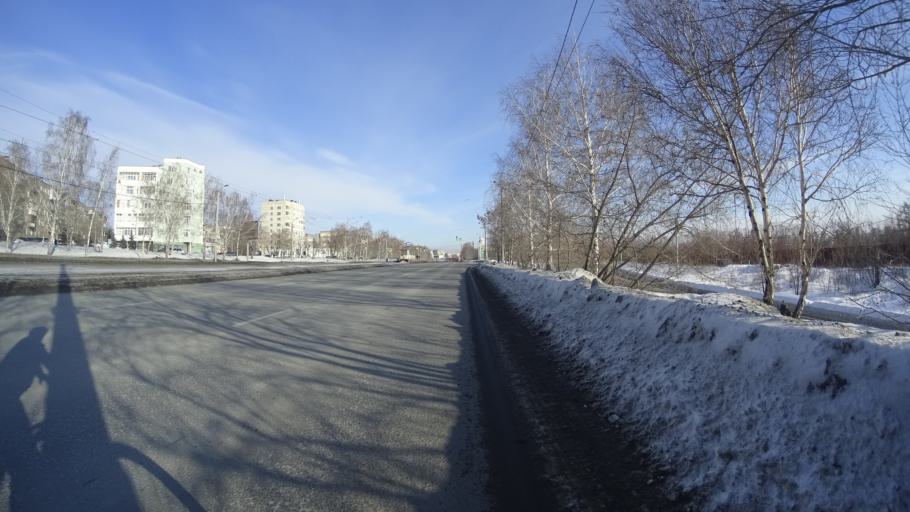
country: RU
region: Chelyabinsk
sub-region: Gorod Chelyabinsk
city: Chelyabinsk
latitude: 55.1889
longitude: 61.3453
